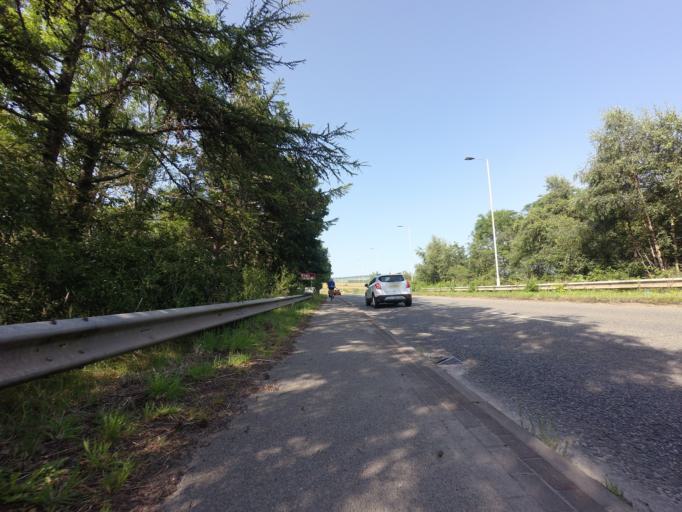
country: GB
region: Scotland
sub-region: Highland
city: Alness
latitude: 57.6828
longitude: -4.2959
